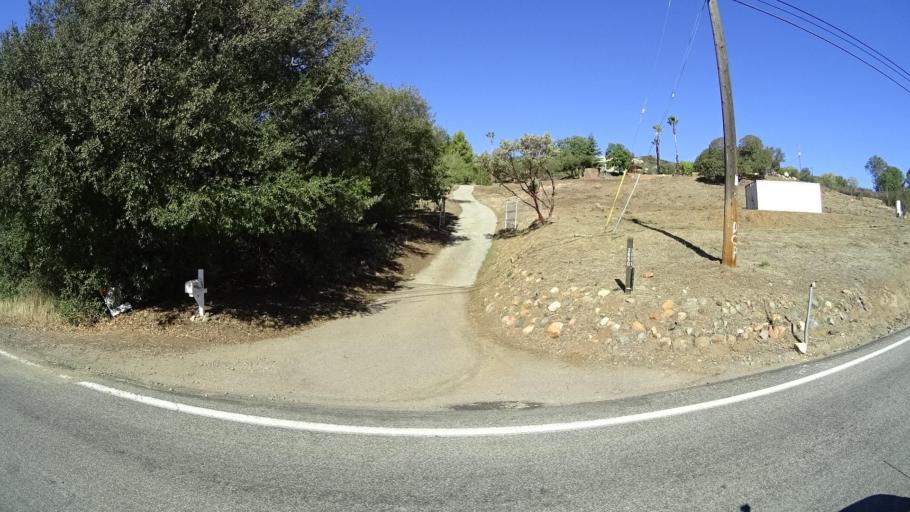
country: US
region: California
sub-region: San Diego County
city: Jamul
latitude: 32.6969
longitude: -116.7474
